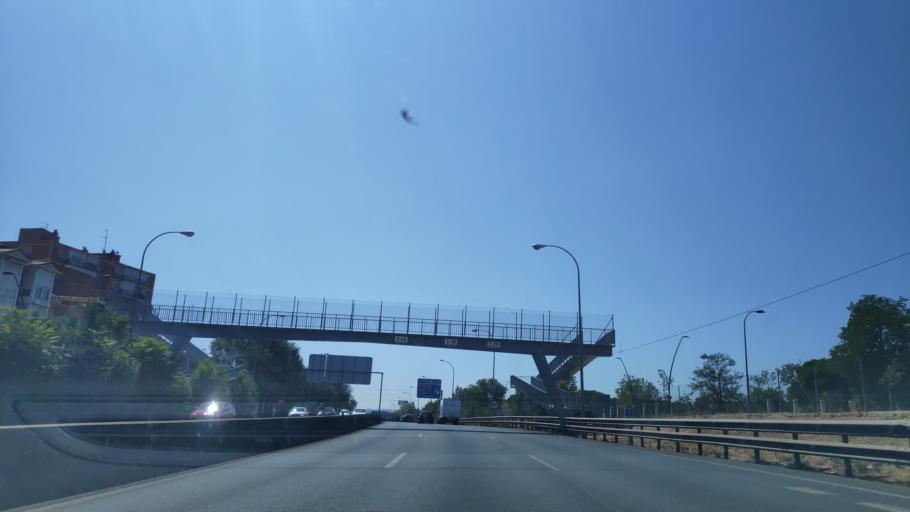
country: ES
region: Madrid
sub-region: Provincia de Madrid
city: Getafe
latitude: 40.3098
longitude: -3.7406
